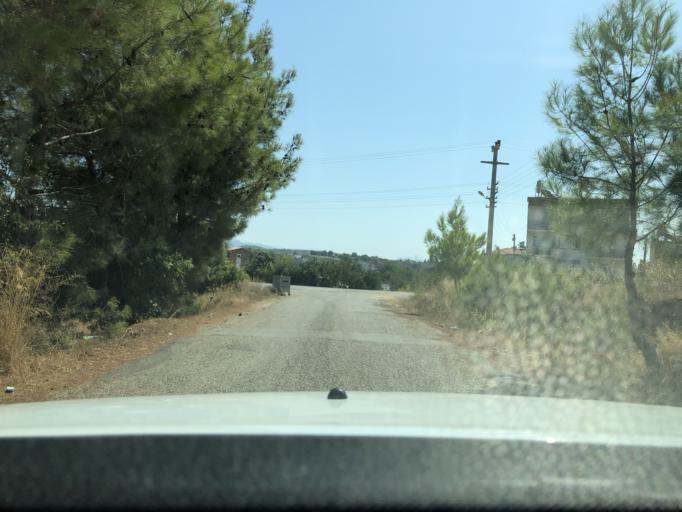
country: TR
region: Antalya
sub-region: Manavgat
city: Manavgat
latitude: 36.8041
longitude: 31.4755
